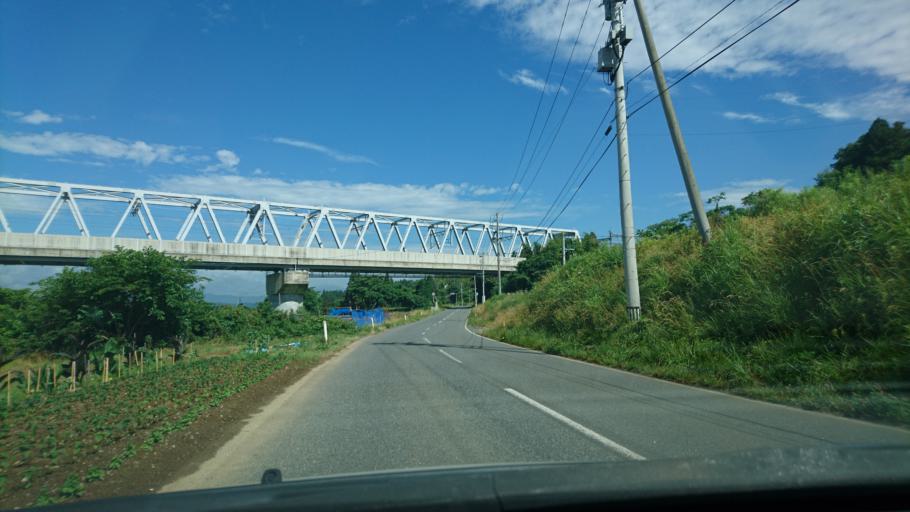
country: JP
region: Iwate
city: Ichinoseki
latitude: 38.9751
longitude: 141.1577
